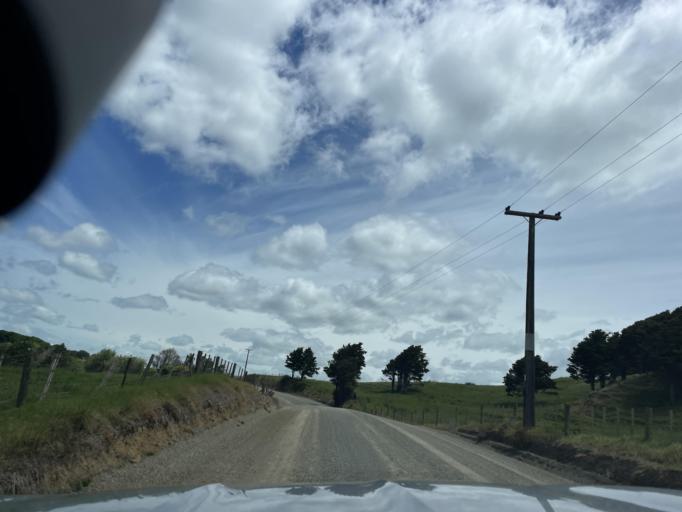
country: NZ
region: Auckland
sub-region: Auckland
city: Wellsford
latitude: -36.1508
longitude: 174.2850
